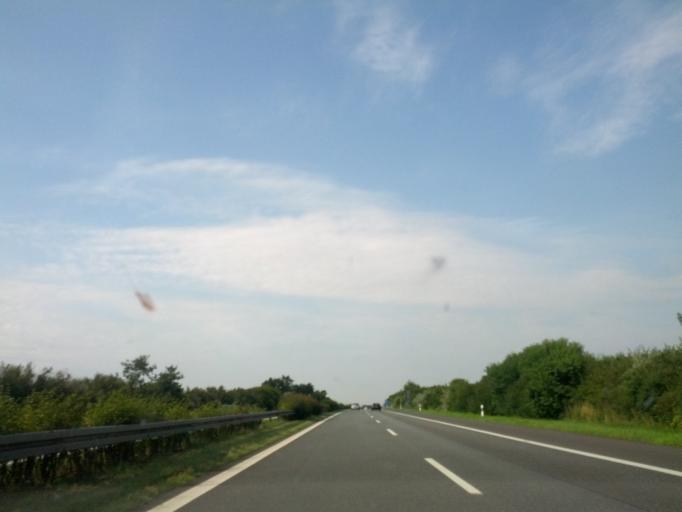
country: DE
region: Mecklenburg-Vorpommern
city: Laage
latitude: 53.8700
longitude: 12.2590
